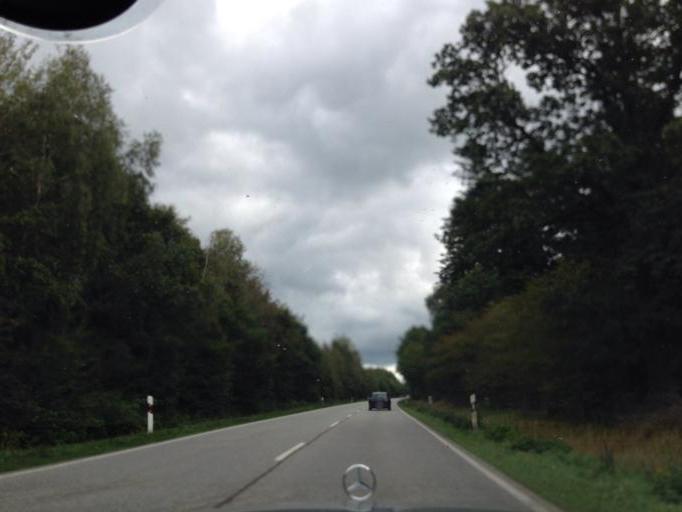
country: DE
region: Schleswig-Holstein
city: Leck
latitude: 54.7515
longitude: 9.0093
